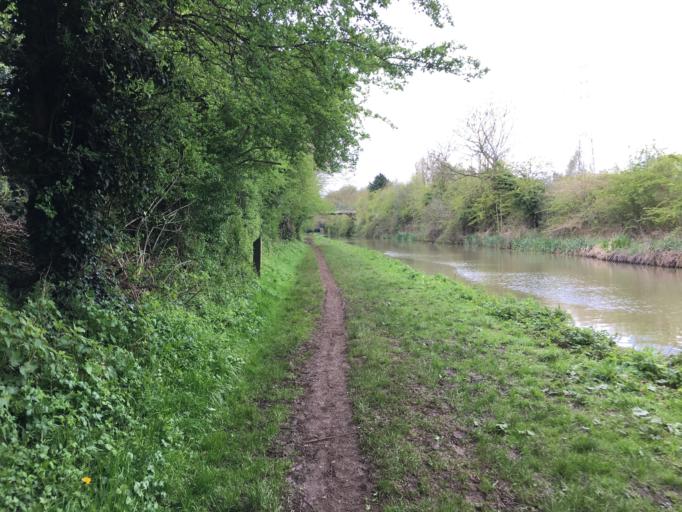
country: GB
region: England
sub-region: Warwickshire
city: Rugby
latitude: 52.3891
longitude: -1.2646
